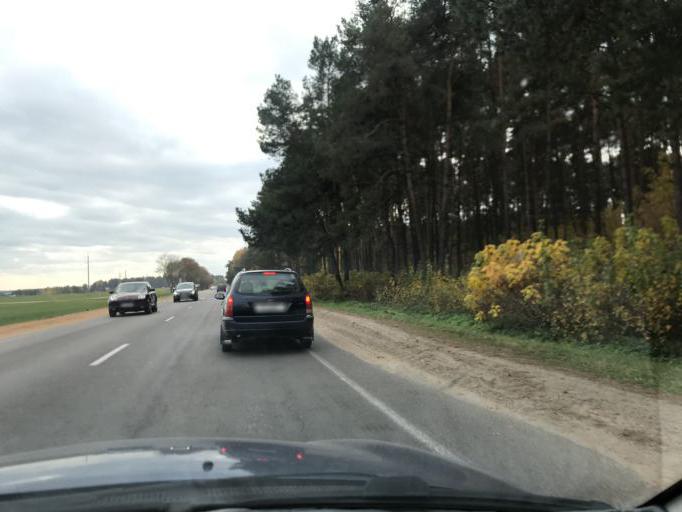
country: BY
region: Grodnenskaya
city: Lida
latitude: 53.8790
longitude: 25.2571
